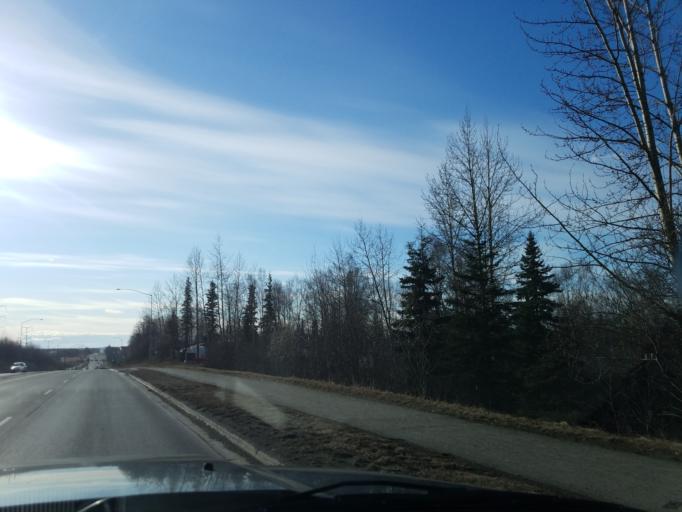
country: US
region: Alaska
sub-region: Anchorage Municipality
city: Anchorage
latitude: 61.1808
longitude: -149.7580
